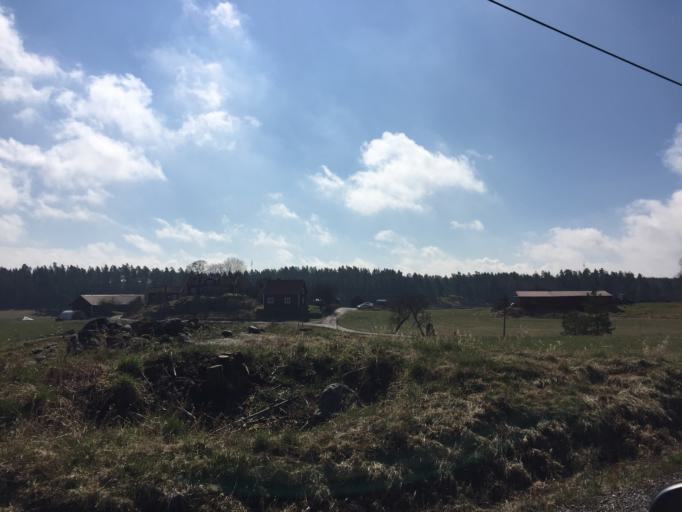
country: SE
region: Soedermanland
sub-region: Gnesta Kommun
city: Gnesta
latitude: 59.0374
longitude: 17.2346
